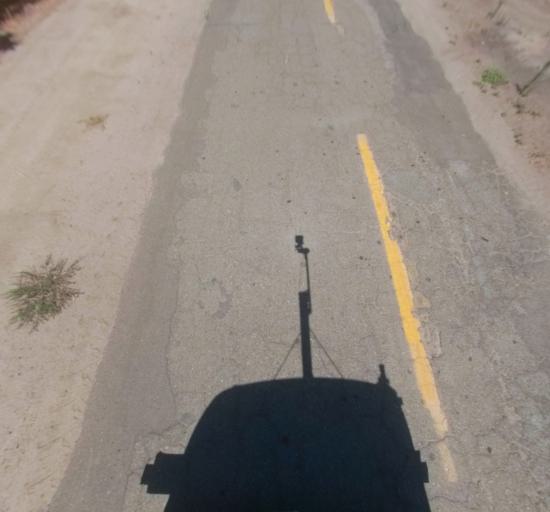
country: US
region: California
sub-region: Madera County
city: Chowchilla
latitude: 37.0327
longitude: -120.2976
